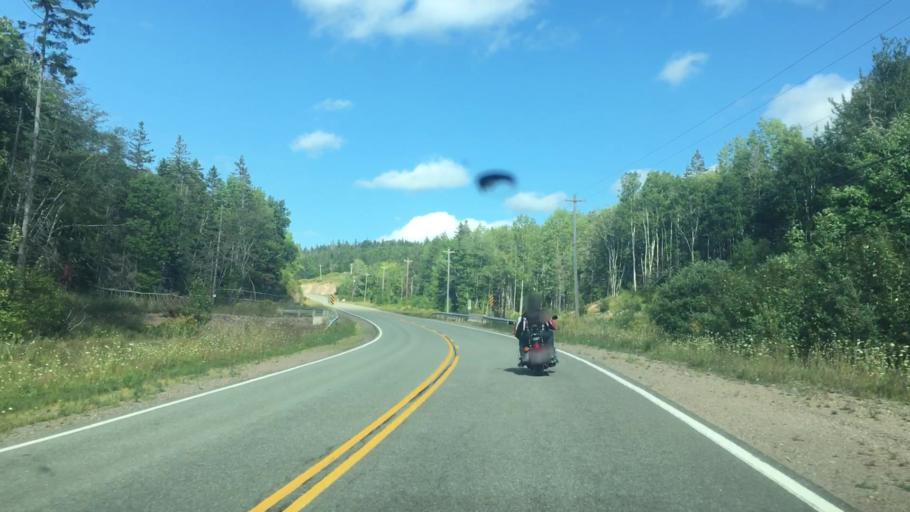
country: CA
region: Nova Scotia
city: Sydney
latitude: 45.8498
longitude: -60.6395
